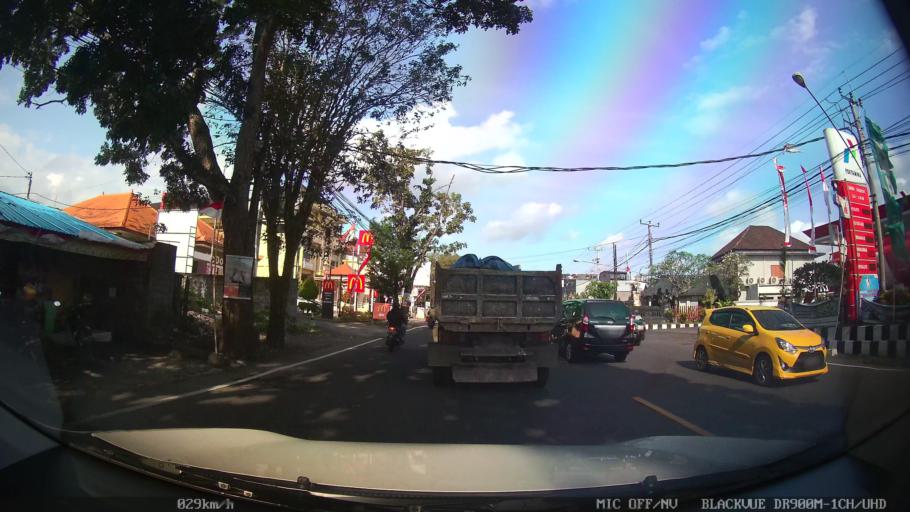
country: ID
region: Bali
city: Tabanan
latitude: -8.5518
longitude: 115.1303
